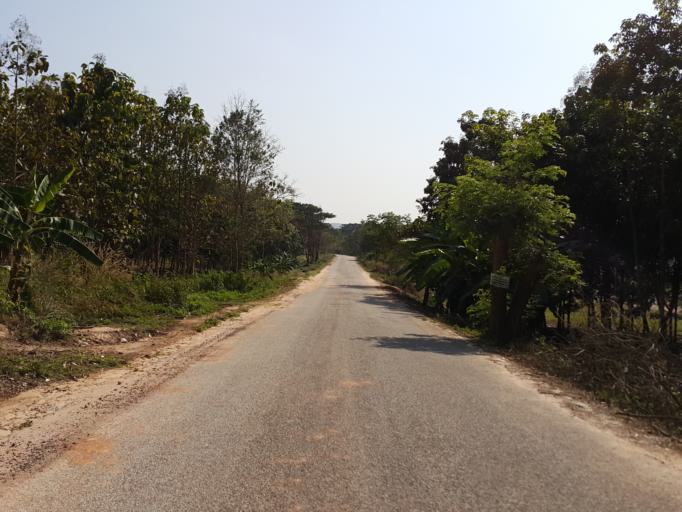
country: TH
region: Lampang
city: Wang Nuea
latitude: 19.0071
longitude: 99.6225
